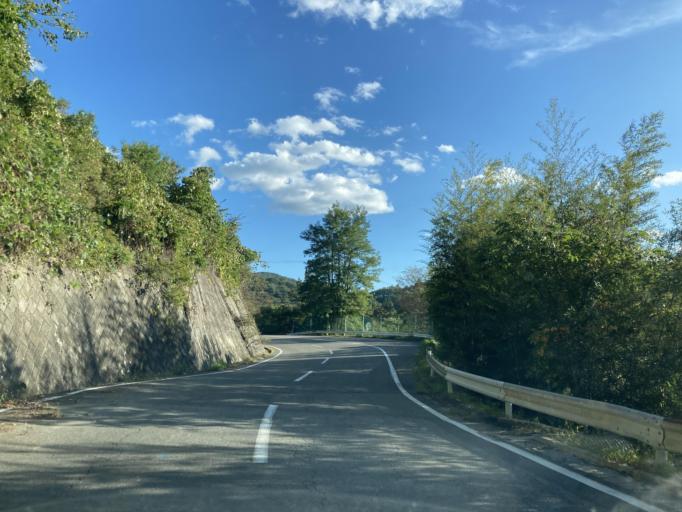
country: JP
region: Nagano
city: Omachi
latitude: 36.4404
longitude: 137.9933
